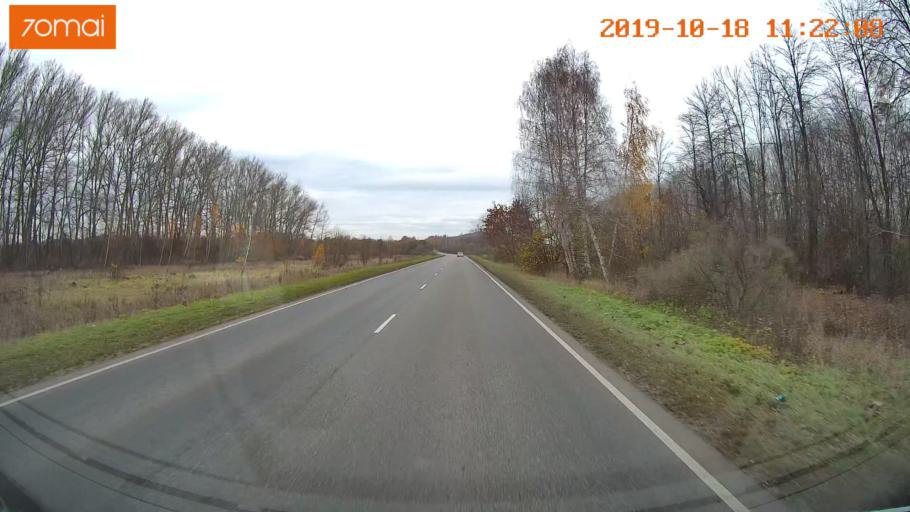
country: RU
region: Tula
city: Kimovsk
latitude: 54.0834
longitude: 38.5761
